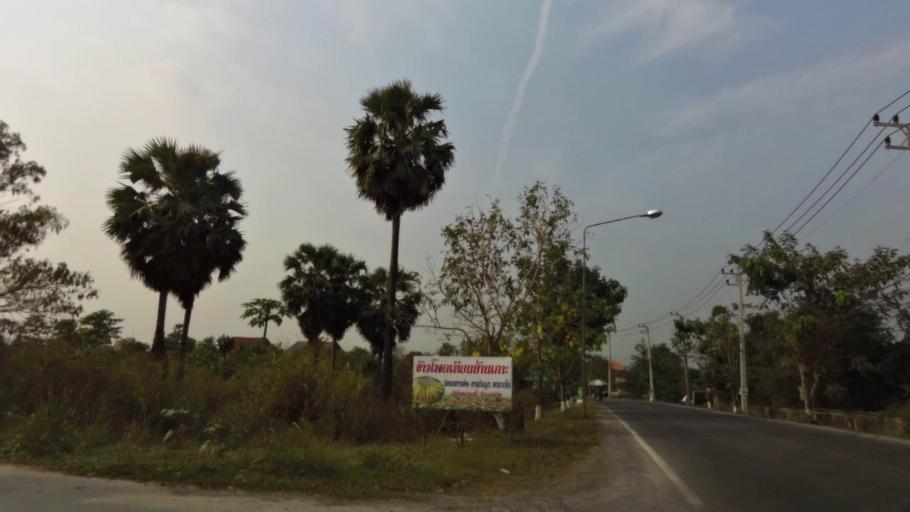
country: TH
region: Phra Nakhon Si Ayutthaya
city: Phra Nakhon Si Ayutthaya
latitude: 14.3418
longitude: 100.5741
